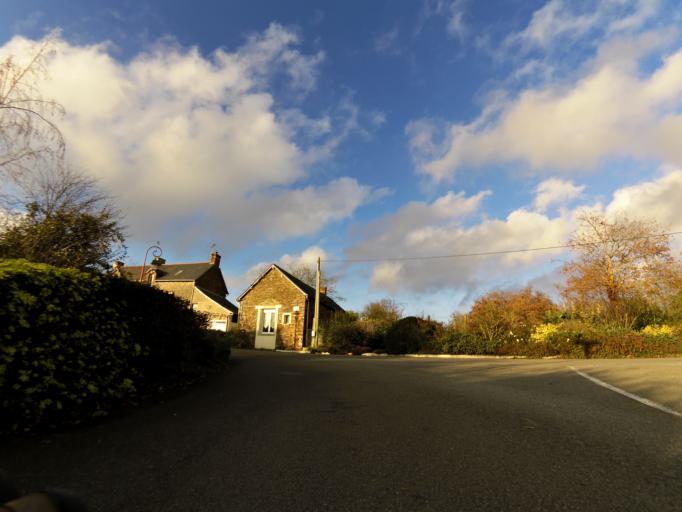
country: FR
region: Brittany
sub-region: Departement d'Ille-et-Vilaine
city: Pance
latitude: 47.8958
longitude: -1.6065
